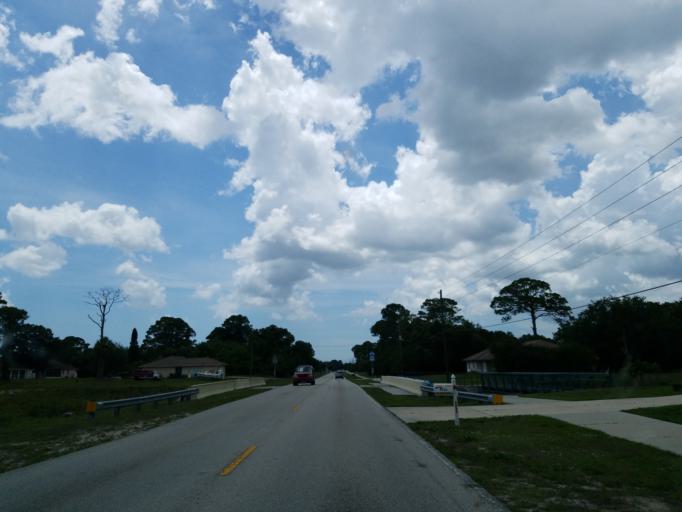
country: US
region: Florida
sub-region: Sarasota County
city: North Port
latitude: 27.0688
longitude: -82.1915
